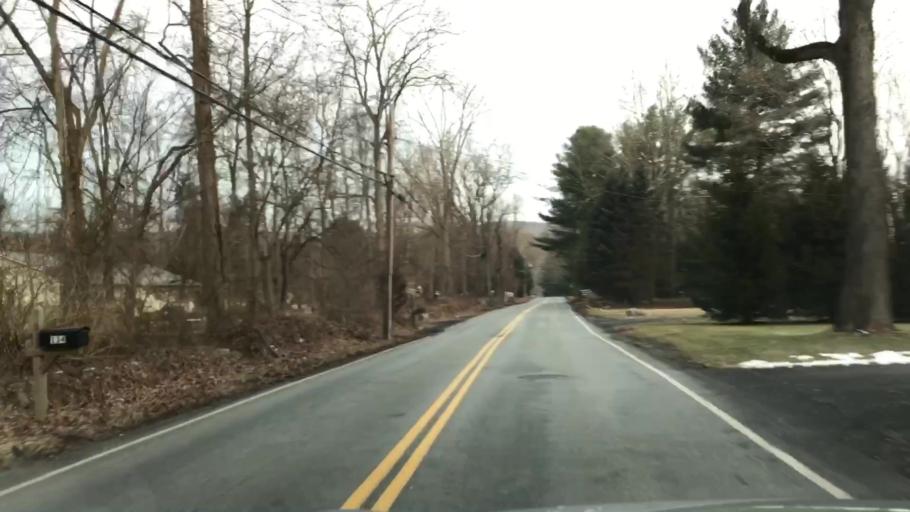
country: US
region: New York
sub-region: Rockland County
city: Viola
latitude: 41.1428
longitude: -74.0980
